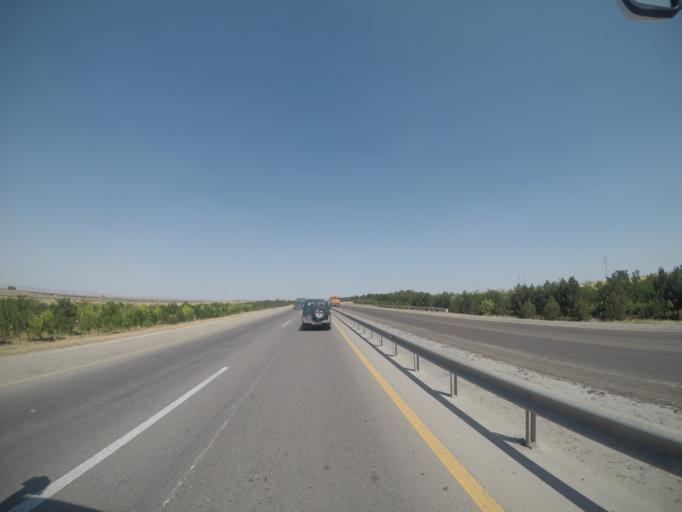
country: AZ
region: Haciqabul
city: Haciqabul
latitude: 40.0464
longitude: 49.0011
